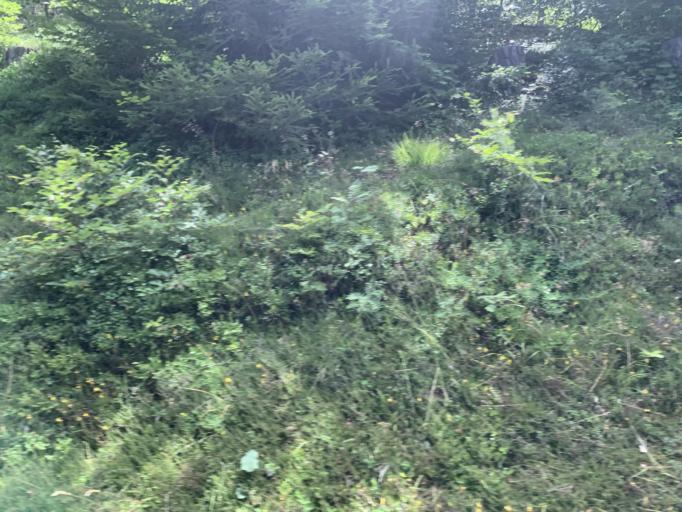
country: IT
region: Trentino-Alto Adige
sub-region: Bolzano
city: Renon - Ritten
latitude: 46.5284
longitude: 11.4345
